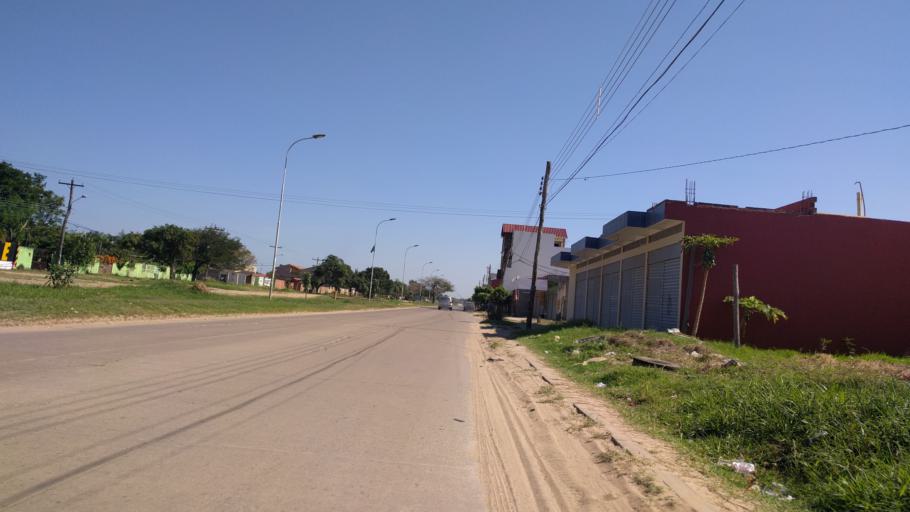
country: BO
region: Santa Cruz
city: Santa Cruz de la Sierra
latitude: -17.8578
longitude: -63.1883
